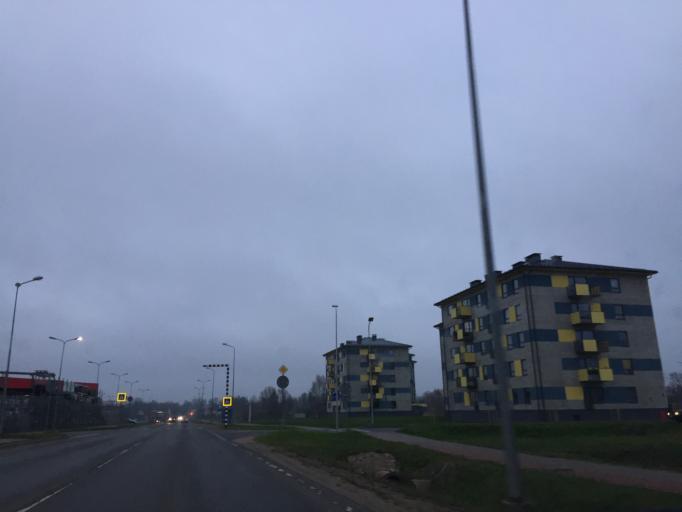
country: LV
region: Valmieras Rajons
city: Valmiera
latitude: 57.5414
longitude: 25.3967
